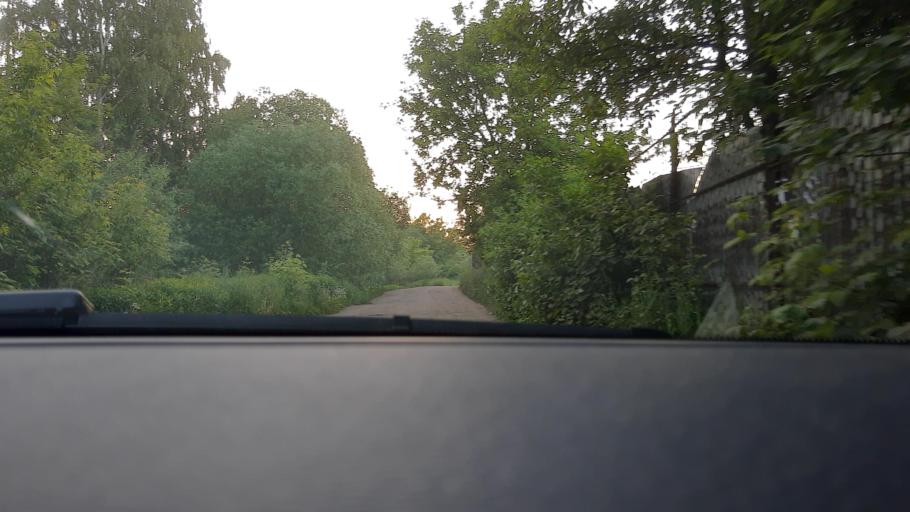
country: RU
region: Nizjnij Novgorod
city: Burevestnik
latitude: 56.2137
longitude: 43.8386
